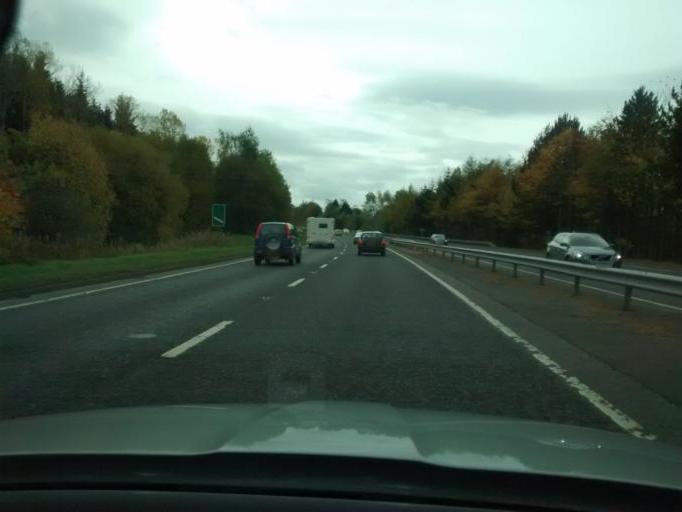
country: GB
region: Scotland
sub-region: Perth and Kinross
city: Luncarty
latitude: 56.4126
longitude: -3.4790
